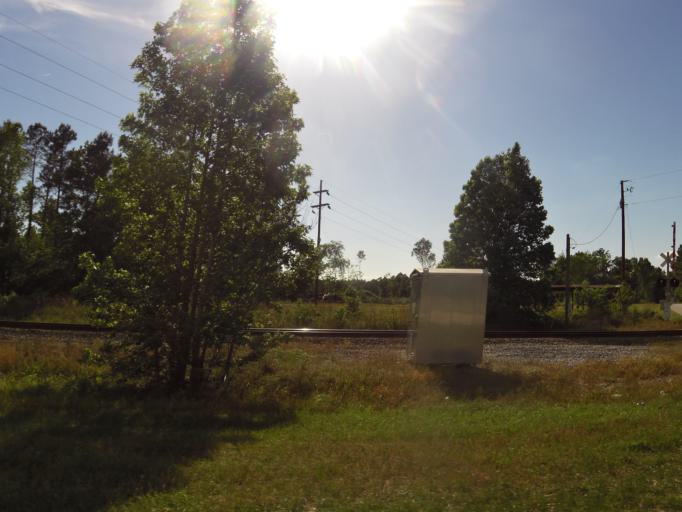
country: US
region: South Carolina
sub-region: Allendale County
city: Fairfax
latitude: 32.9209
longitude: -81.2375
